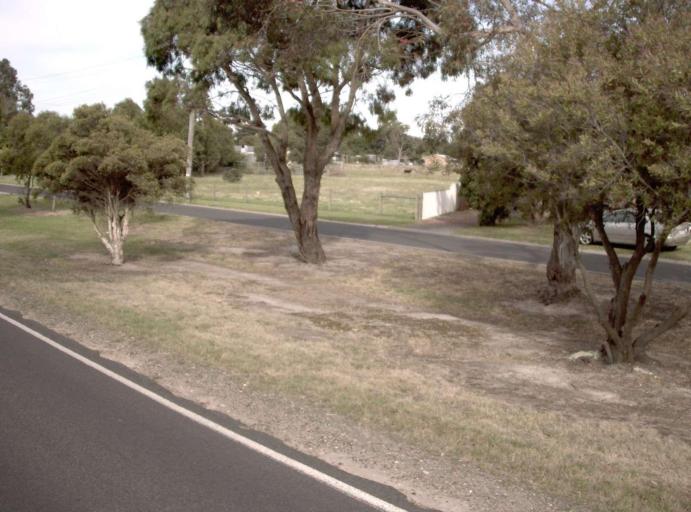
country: AU
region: Victoria
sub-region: Latrobe
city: Traralgon
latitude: -38.1244
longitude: 146.5692
